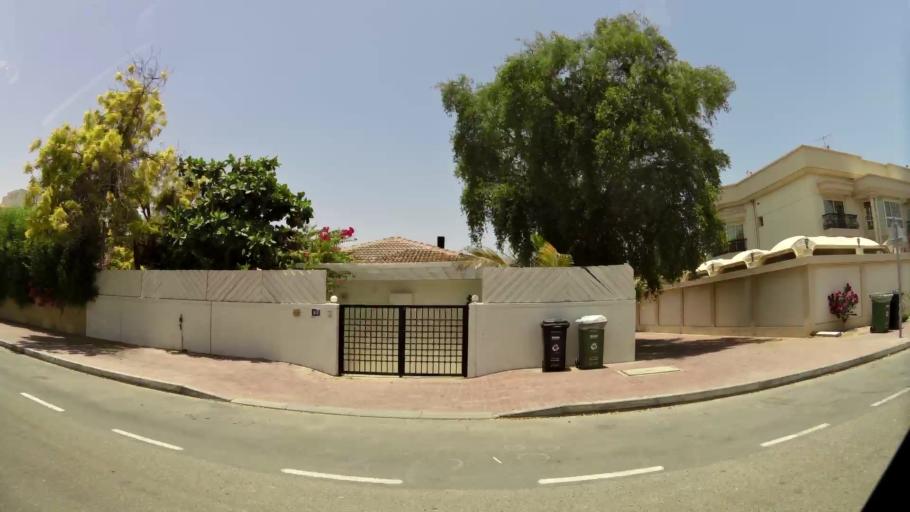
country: AE
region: Dubai
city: Dubai
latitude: 25.1723
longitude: 55.2251
